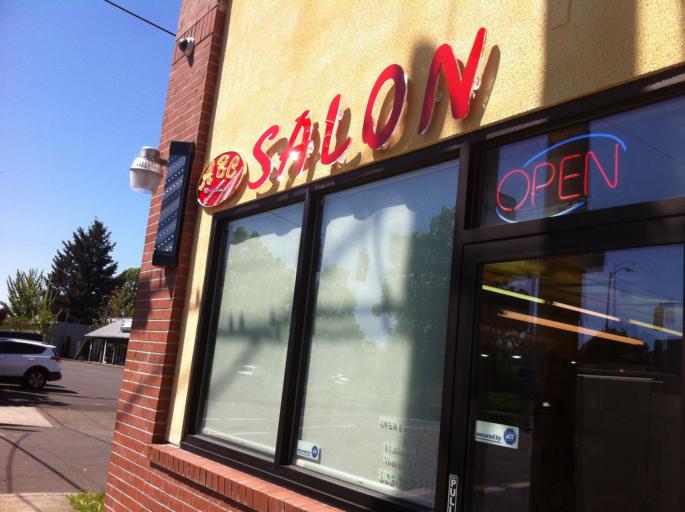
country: US
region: Oregon
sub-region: Multnomah County
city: Lents
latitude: 45.4976
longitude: -122.5965
